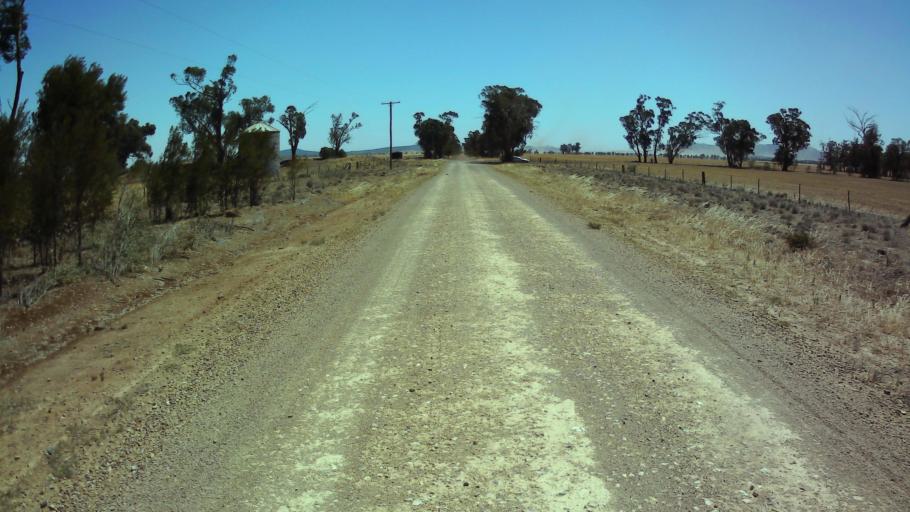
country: AU
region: New South Wales
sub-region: Forbes
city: Forbes
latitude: -33.6809
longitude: 147.7104
